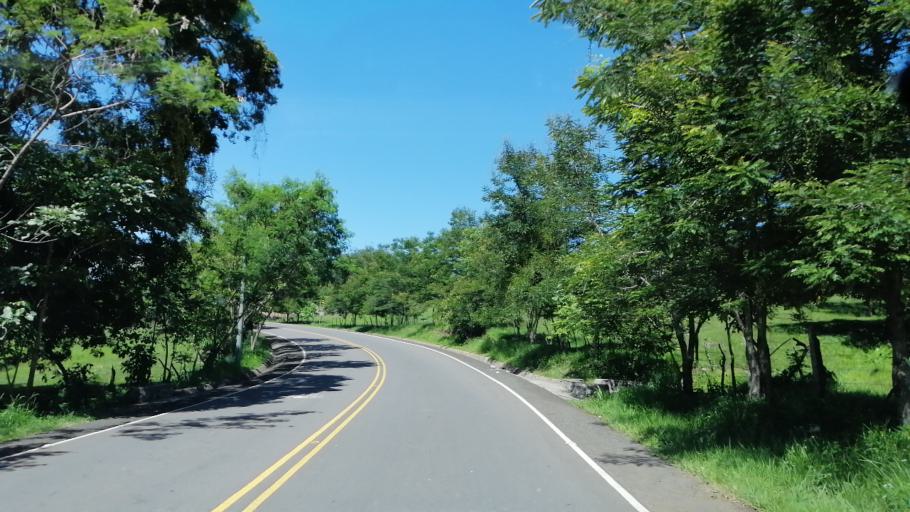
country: SV
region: Morazan
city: Cacaopera
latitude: 13.8091
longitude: -88.1560
